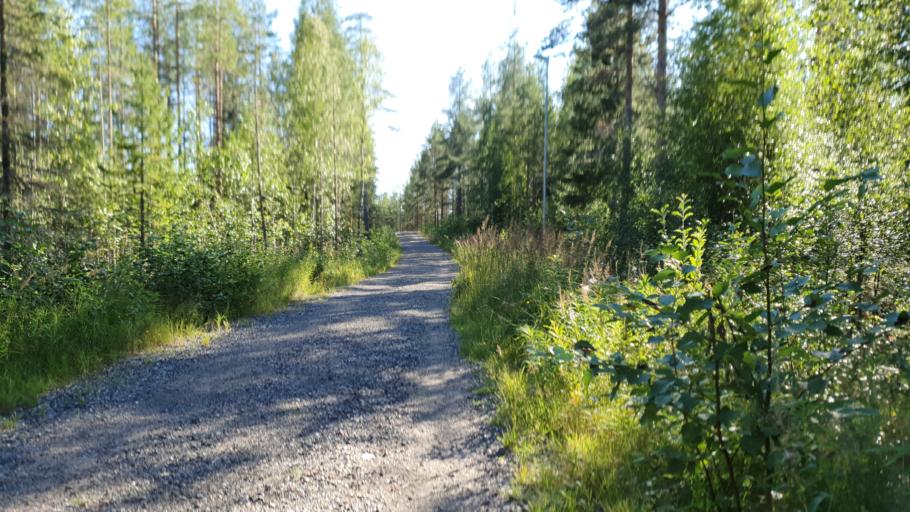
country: FI
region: Kainuu
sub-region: Kehys-Kainuu
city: Kuhmo
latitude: 64.1113
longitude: 29.5049
